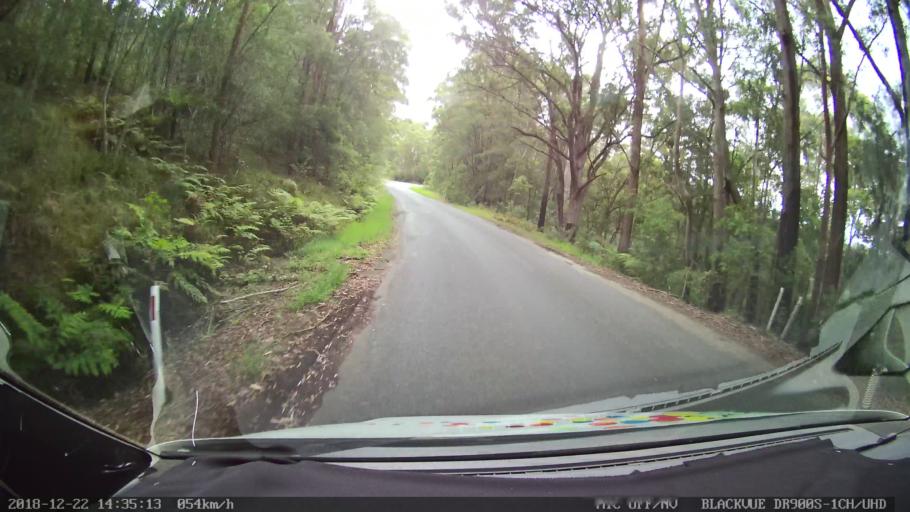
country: AU
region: New South Wales
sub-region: Bellingen
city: Dorrigo
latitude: -30.1224
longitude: 152.6154
